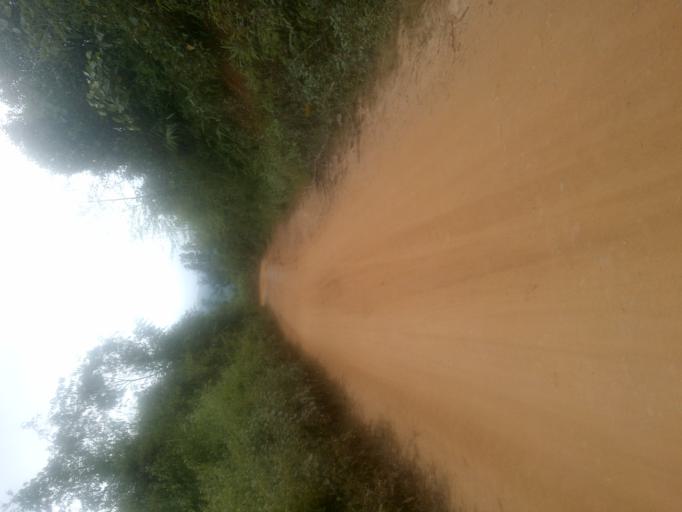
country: LA
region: Xiangkhoang
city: Muang Phonsavan
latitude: 19.3383
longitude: 103.5021
